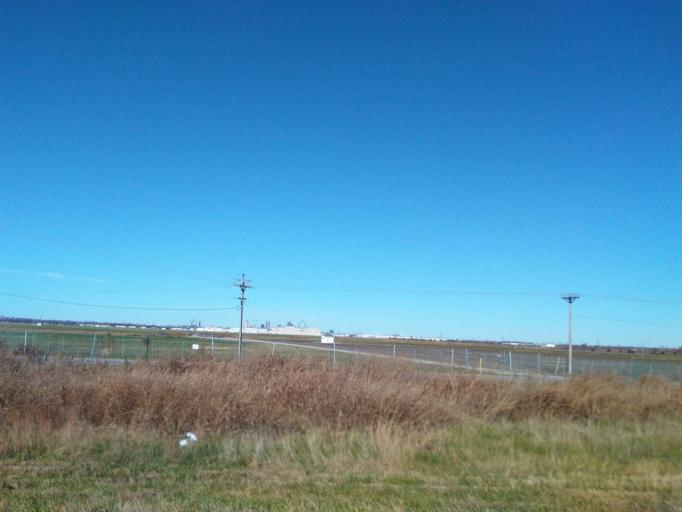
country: US
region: Illinois
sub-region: Saint Clair County
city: Centreville
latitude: 38.5595
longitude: -90.1411
